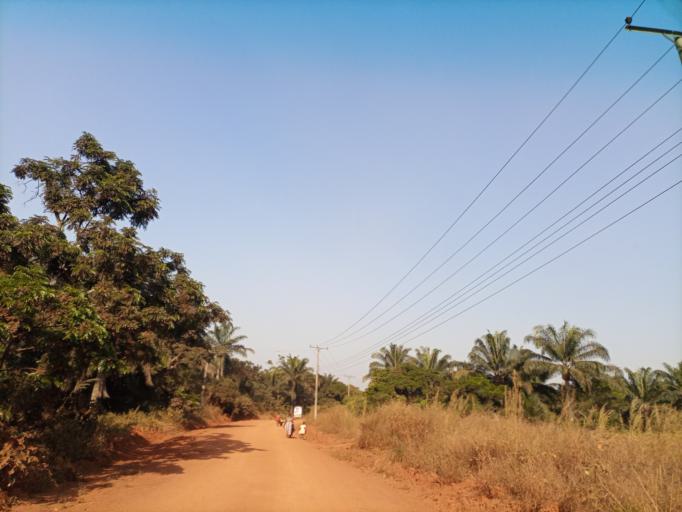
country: NG
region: Enugu
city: Opi
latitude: 6.7773
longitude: 7.3869
